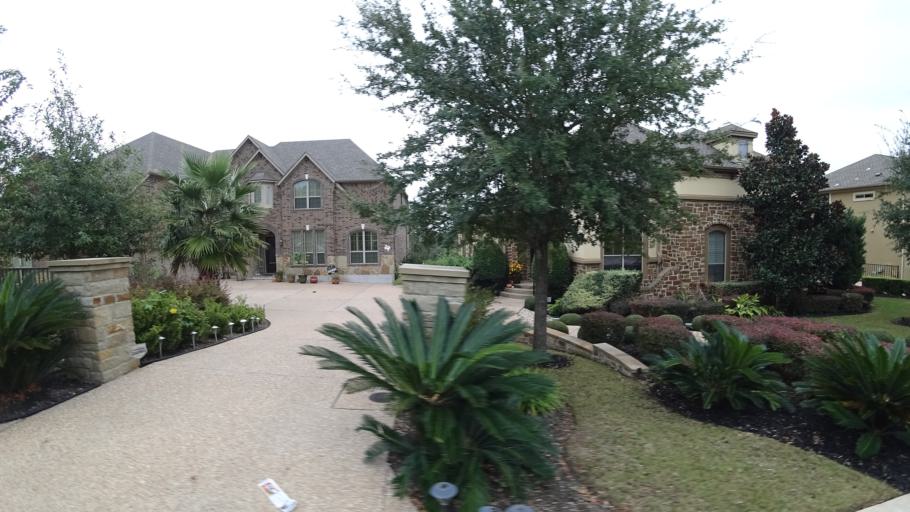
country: US
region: Texas
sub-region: Travis County
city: Bee Cave
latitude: 30.3421
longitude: -97.9066
